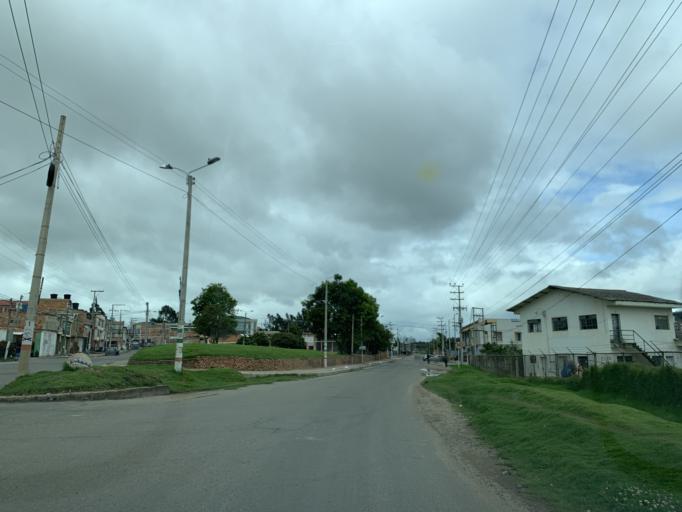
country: CO
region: Boyaca
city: Tunja
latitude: 5.5620
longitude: -73.3472
